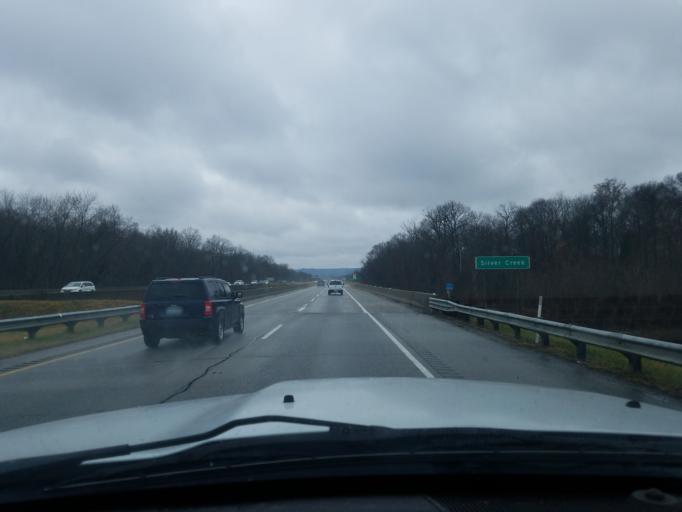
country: US
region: Indiana
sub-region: Clark County
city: Clarksville
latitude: 38.3453
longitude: -85.7680
